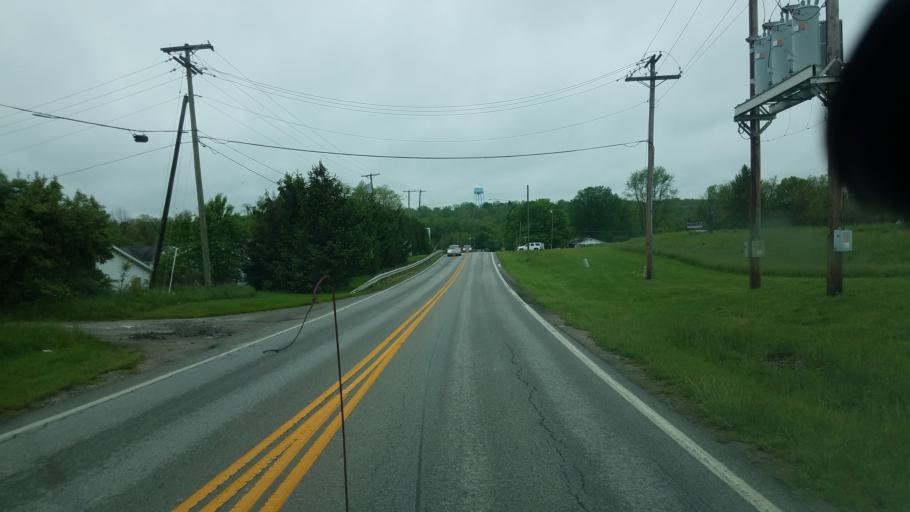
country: US
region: Ohio
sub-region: Highland County
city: Hillsboro
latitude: 39.2192
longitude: -83.6180
